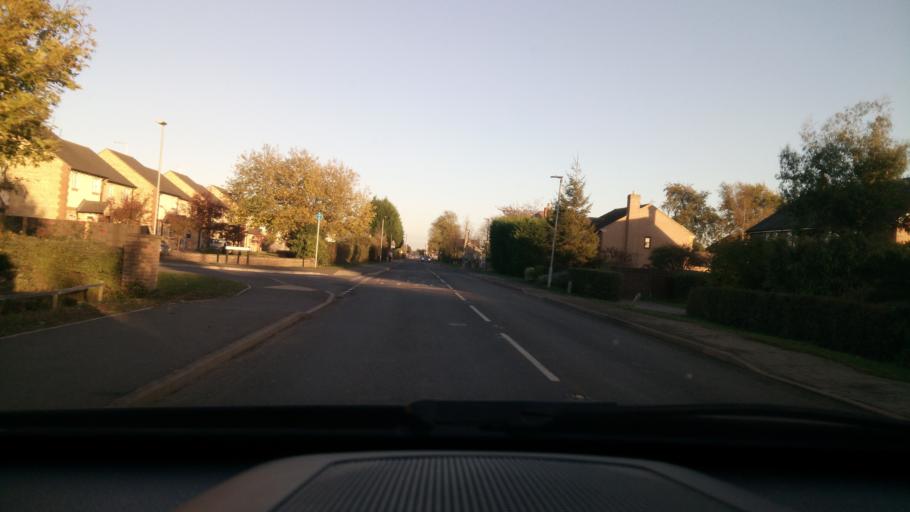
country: GB
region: England
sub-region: Peterborough
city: Helpston
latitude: 52.6359
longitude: -0.3351
